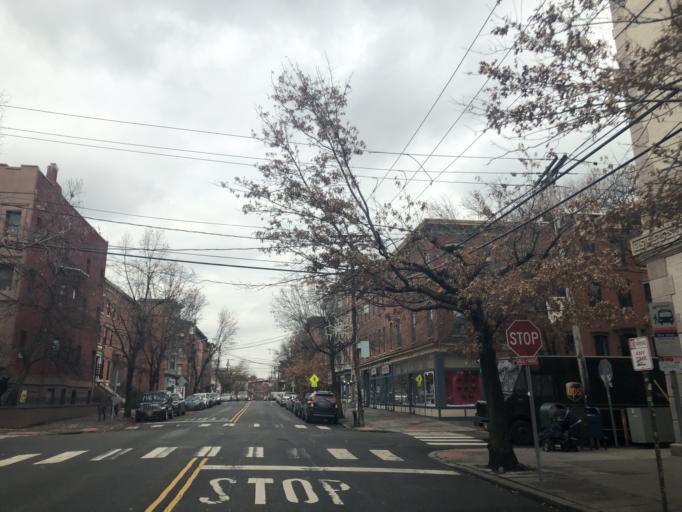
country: US
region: New Jersey
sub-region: Hudson County
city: Hoboken
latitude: 40.7191
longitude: -74.0476
